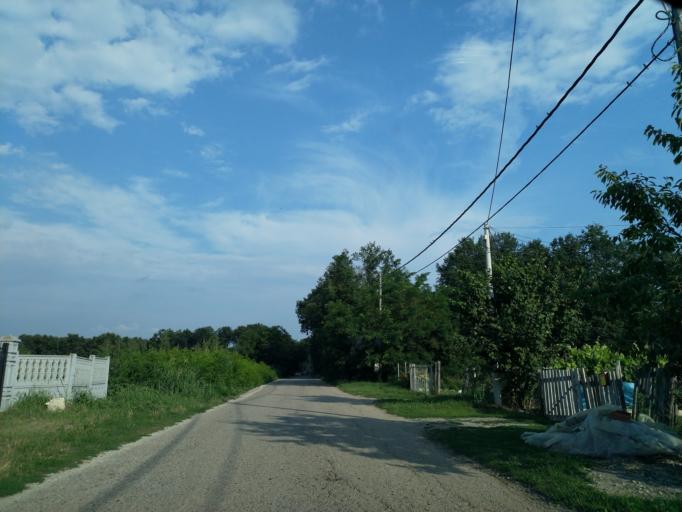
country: RS
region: Central Serbia
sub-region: Pomoravski Okrug
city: Jagodina
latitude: 43.9846
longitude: 21.2189
